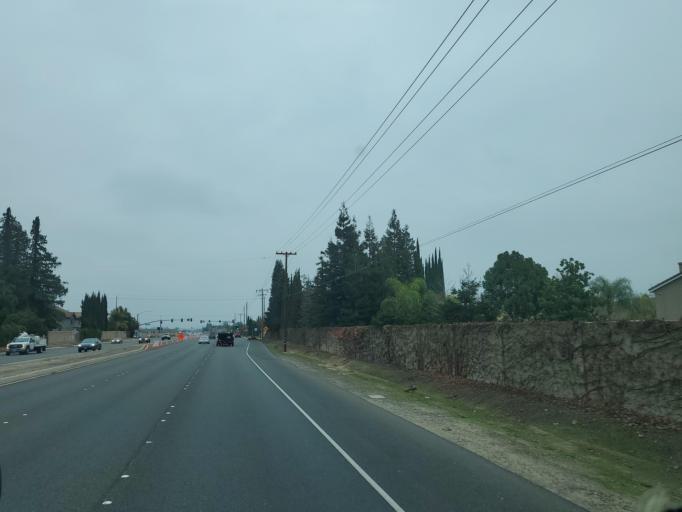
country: US
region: California
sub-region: Stanislaus County
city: Del Rio
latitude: 37.7003
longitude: -121.0252
